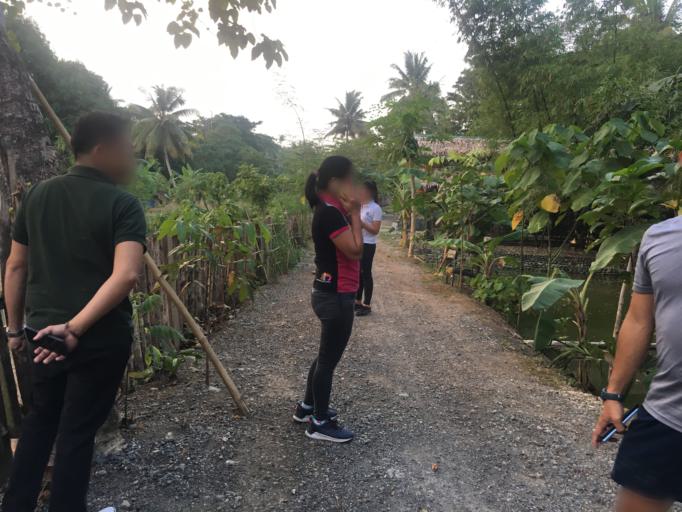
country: PH
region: Davao
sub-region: Province of Davao del Norte
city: Magatos
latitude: 7.6030
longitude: 125.7533
